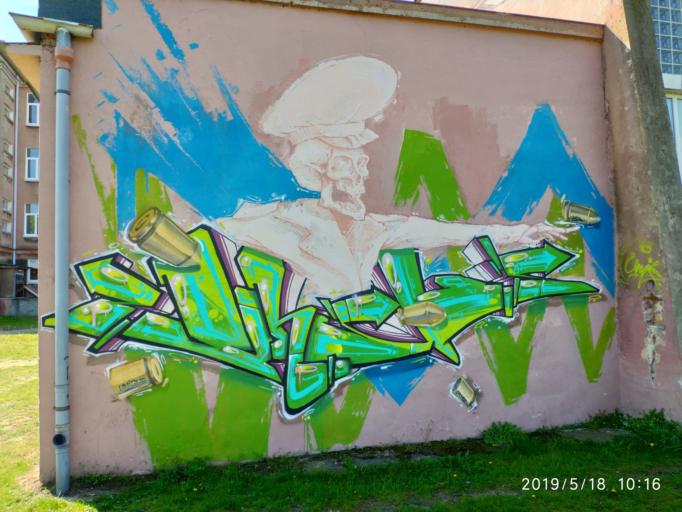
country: PL
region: Lubusz
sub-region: Zielona Gora
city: Zielona Gora
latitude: 51.9465
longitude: 15.5249
